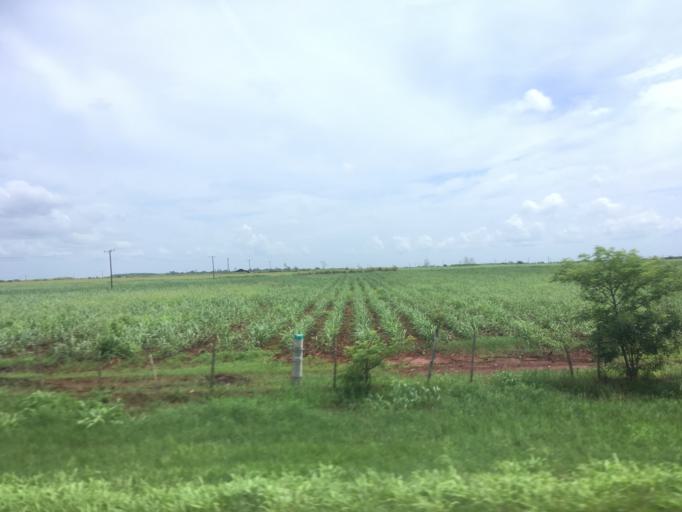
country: CU
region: Matanzas
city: Jovellanos
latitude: 22.7947
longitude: -81.1373
